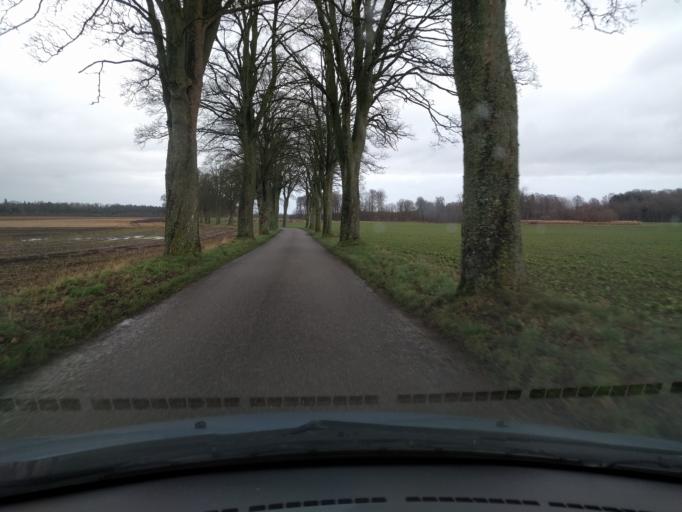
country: DK
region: South Denmark
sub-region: Kerteminde Kommune
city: Langeskov
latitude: 55.3536
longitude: 10.5437
